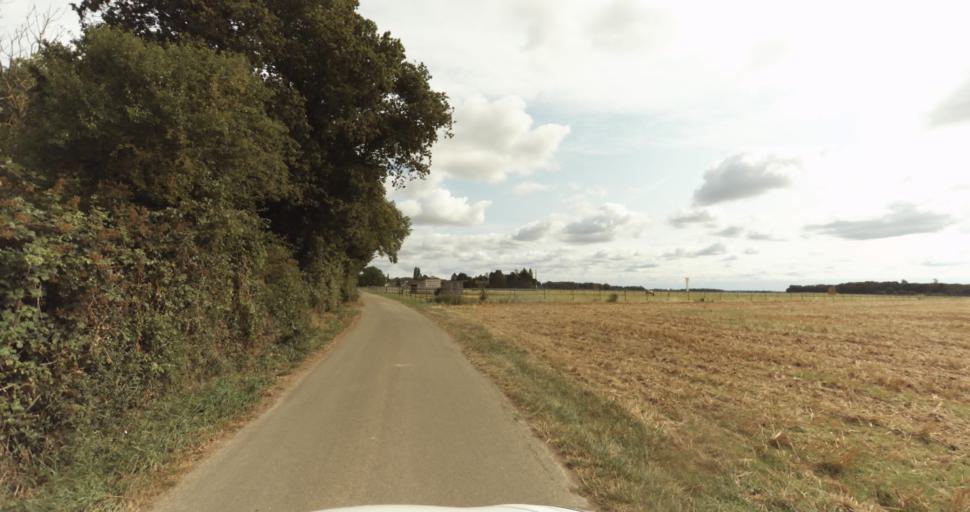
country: FR
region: Haute-Normandie
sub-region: Departement de l'Eure
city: Tillieres-sur-Avre
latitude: 48.7925
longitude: 1.0969
